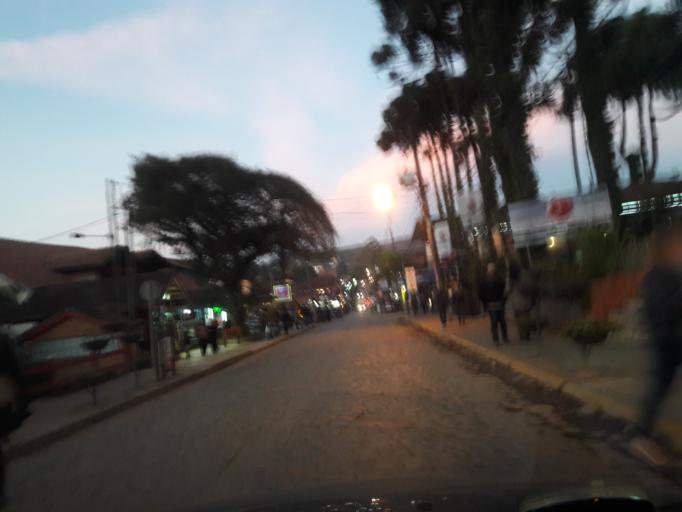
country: BR
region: Minas Gerais
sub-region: Camanducaia
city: Camanducaia
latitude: -22.8633
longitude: -46.0389
